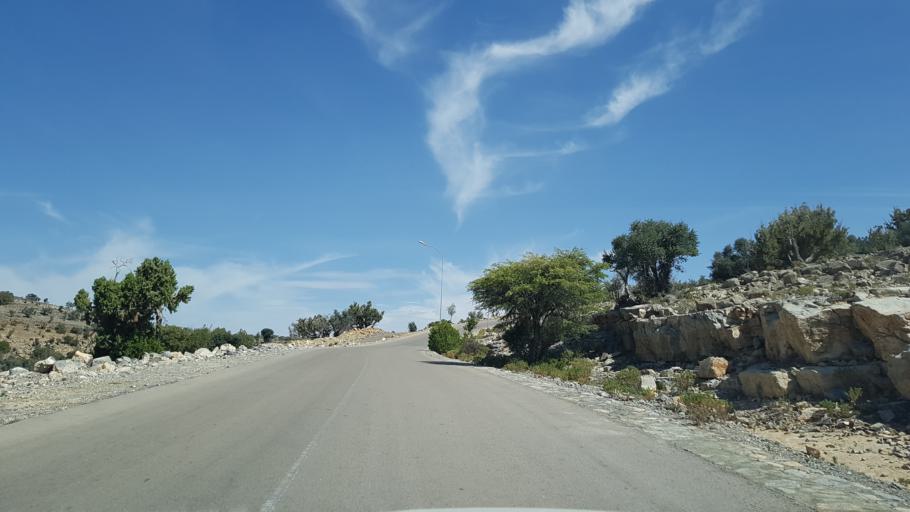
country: OM
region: Al Batinah
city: Bayt al `Awabi
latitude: 23.1341
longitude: 57.5966
